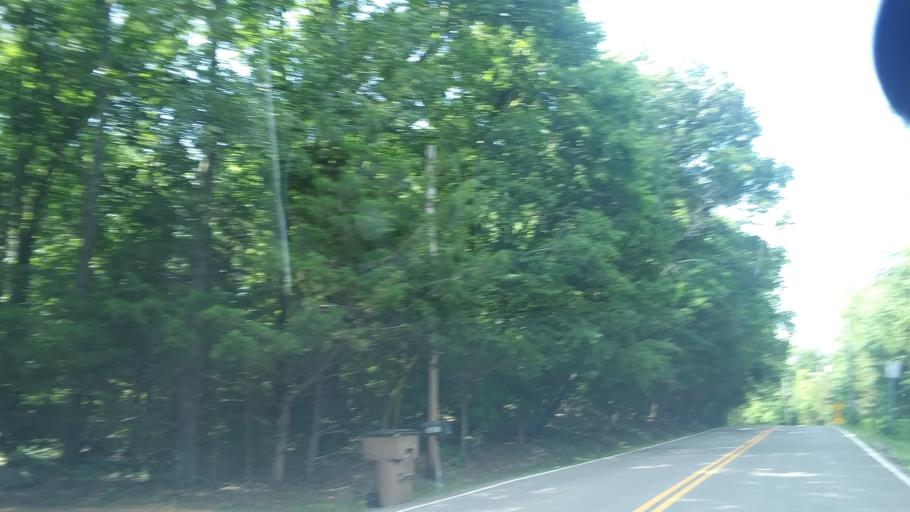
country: US
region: Tennessee
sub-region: Rutherford County
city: La Vergne
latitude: 36.0954
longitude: -86.6340
